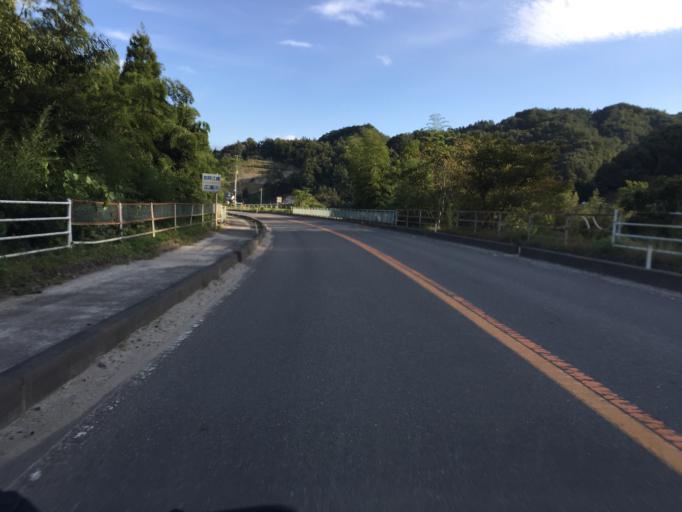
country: JP
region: Fukushima
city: Hobaramachi
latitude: 37.6927
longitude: 140.6091
